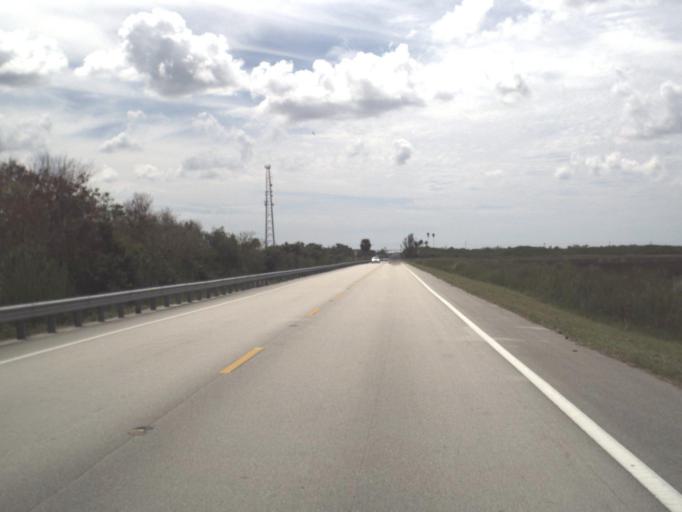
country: US
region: Florida
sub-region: Collier County
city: Marco
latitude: 25.9174
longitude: -81.3605
